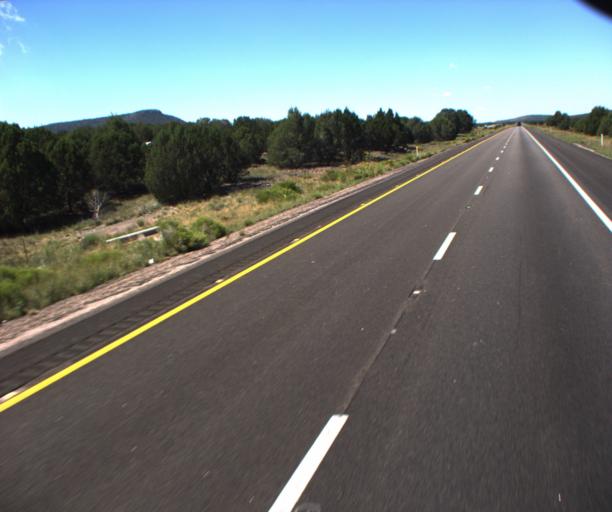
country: US
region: Arizona
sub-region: Mohave County
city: Peach Springs
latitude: 35.2236
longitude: -113.2414
